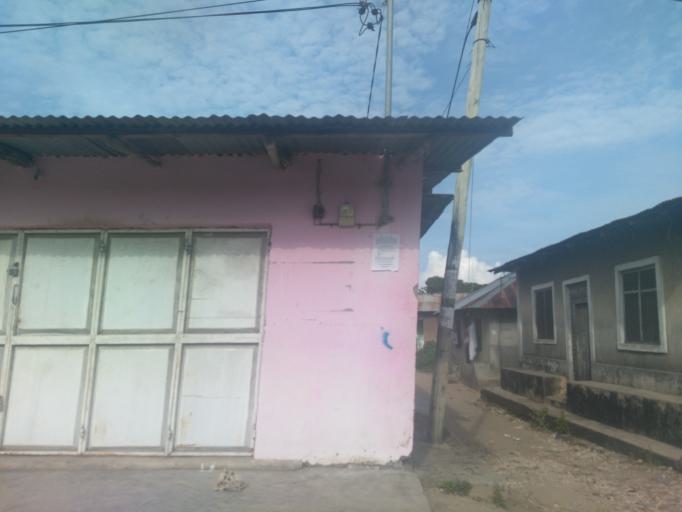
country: TZ
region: Zanzibar Urban/West
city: Zanzibar
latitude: -6.1641
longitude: 39.2095
